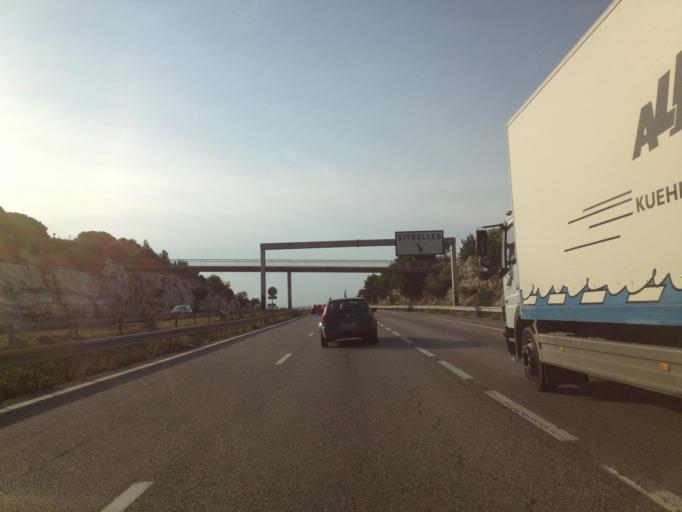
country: FR
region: Provence-Alpes-Cote d'Azur
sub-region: Departement des Bouches-du-Rhone
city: Vitrolles
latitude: 43.4511
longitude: 5.2386
